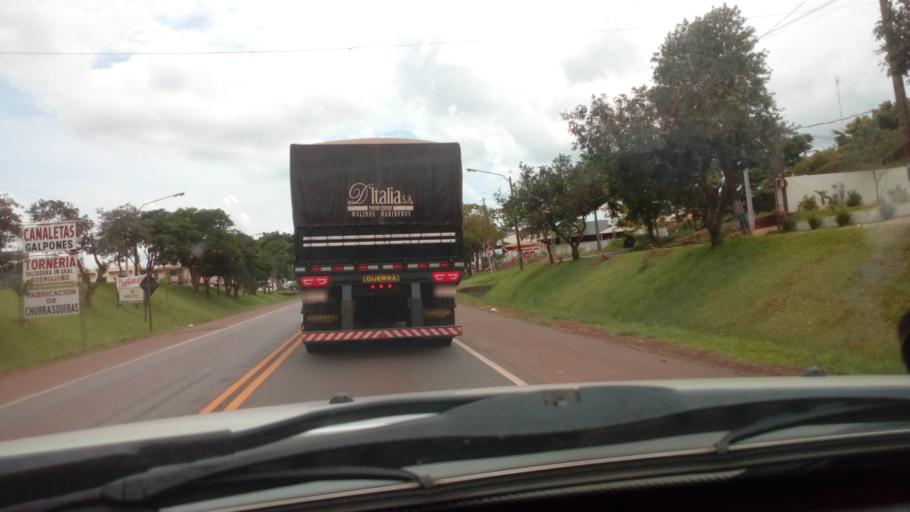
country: PY
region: Alto Parana
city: Santa Rita
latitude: -25.7890
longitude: -55.0834
